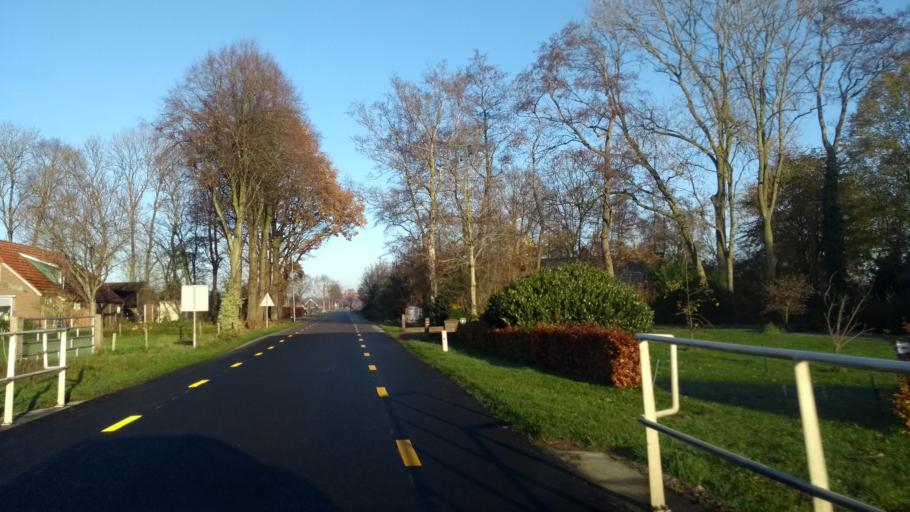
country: NL
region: Overijssel
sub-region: Gemeente Staphorst
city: Staphorst
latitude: 52.5982
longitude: 6.2831
